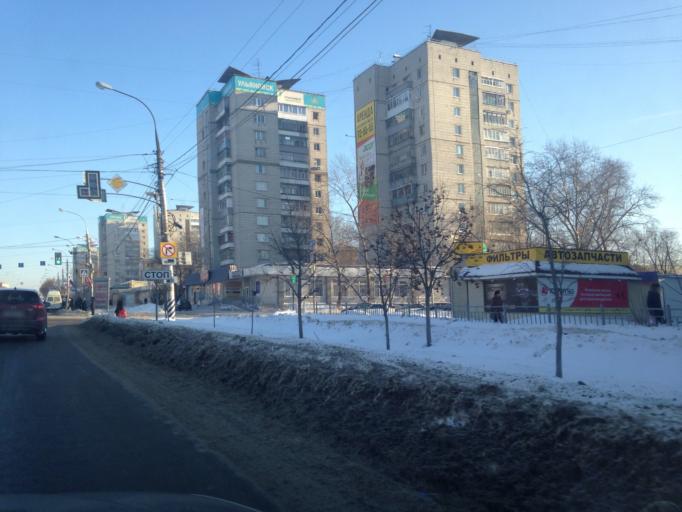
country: RU
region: Ulyanovsk
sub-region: Ulyanovskiy Rayon
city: Ulyanovsk
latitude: 54.3067
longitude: 48.3780
